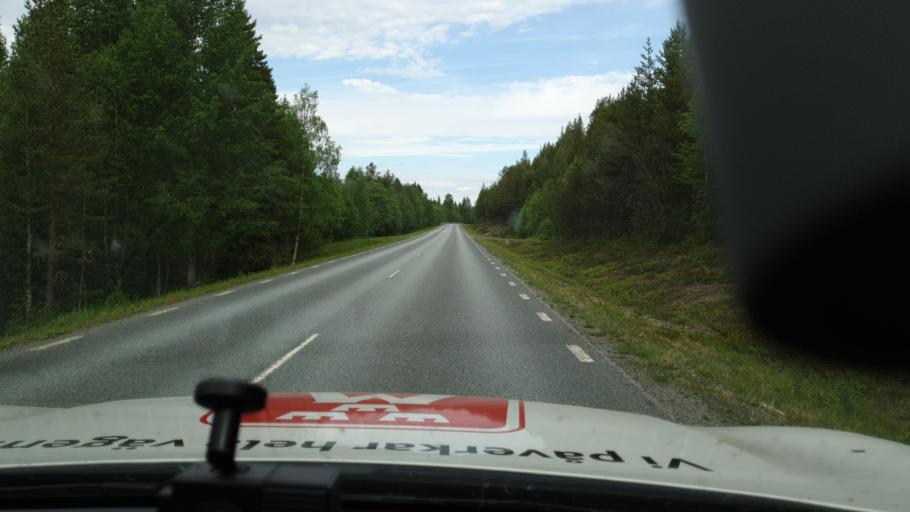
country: SE
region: Vaesterbotten
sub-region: Mala Kommun
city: Mala
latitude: 65.0157
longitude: 18.4462
